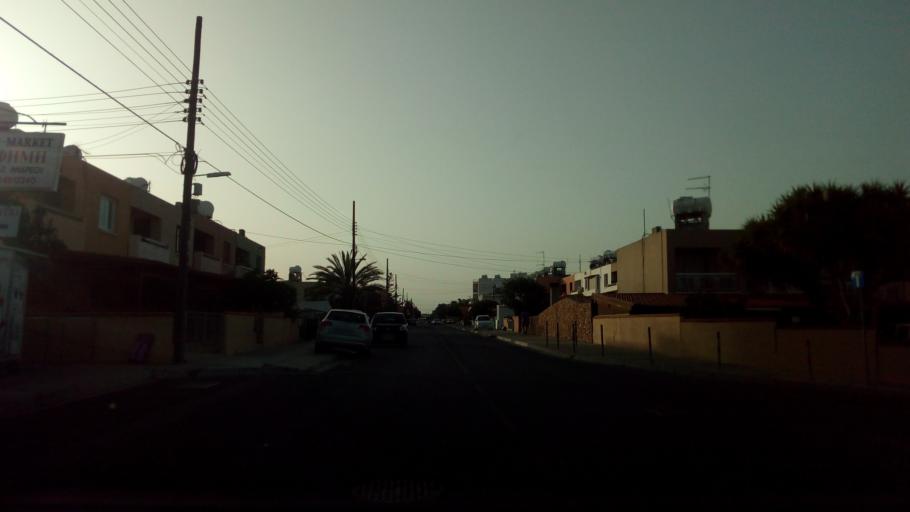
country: CY
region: Larnaka
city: Larnaca
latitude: 34.9344
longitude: 33.6138
